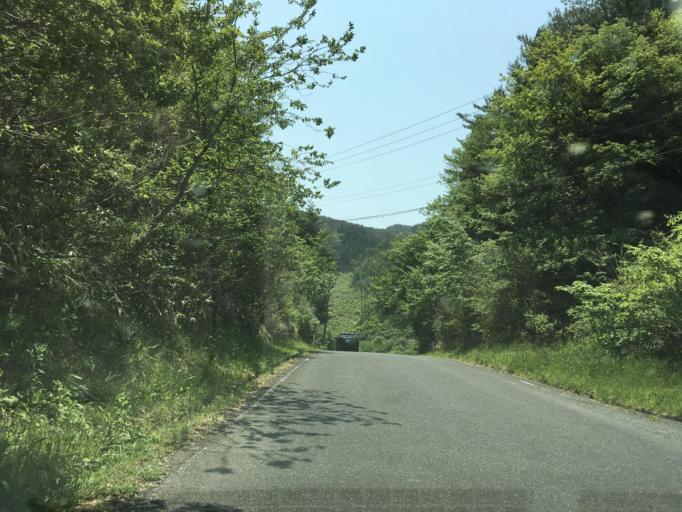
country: JP
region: Iwate
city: Ofunato
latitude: 38.8537
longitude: 141.5113
